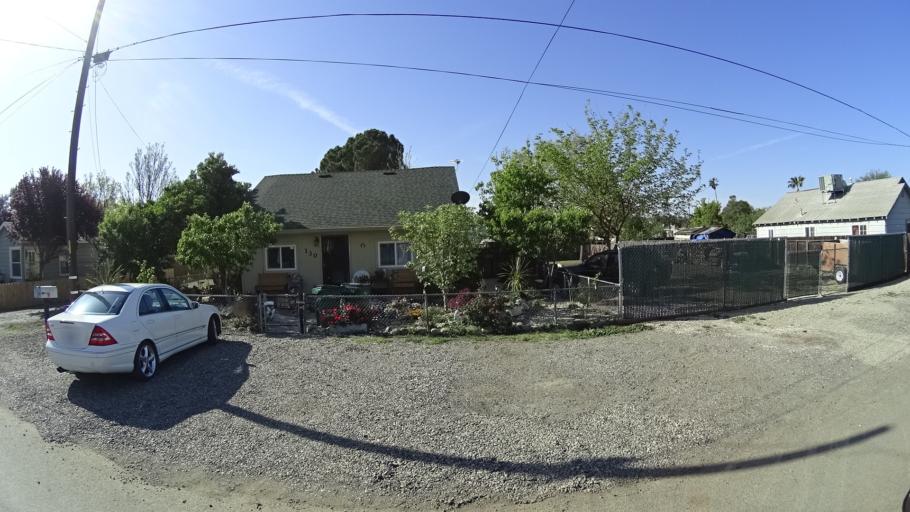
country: US
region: California
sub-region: Glenn County
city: Willows
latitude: 39.5108
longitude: -122.1948
